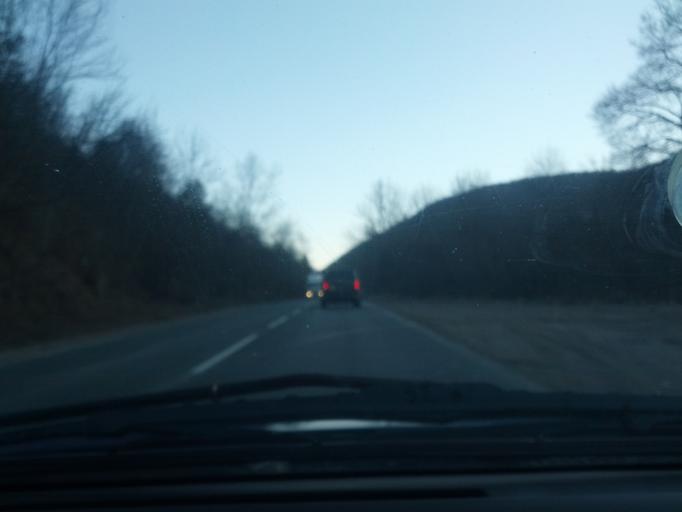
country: BG
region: Vratsa
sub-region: Obshtina Mezdra
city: Mezdra
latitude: 43.1054
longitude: 23.6799
